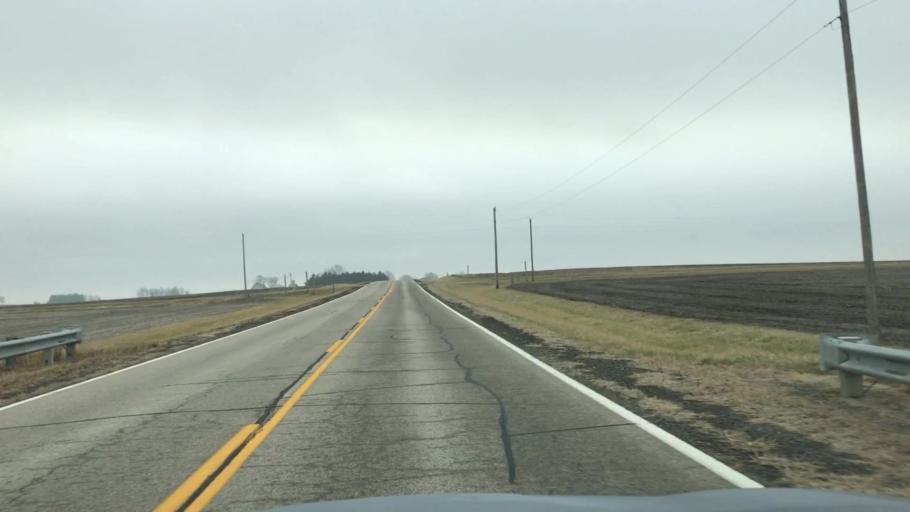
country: US
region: Illinois
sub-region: McLean County
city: Hudson
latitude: 40.6213
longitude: -88.9456
